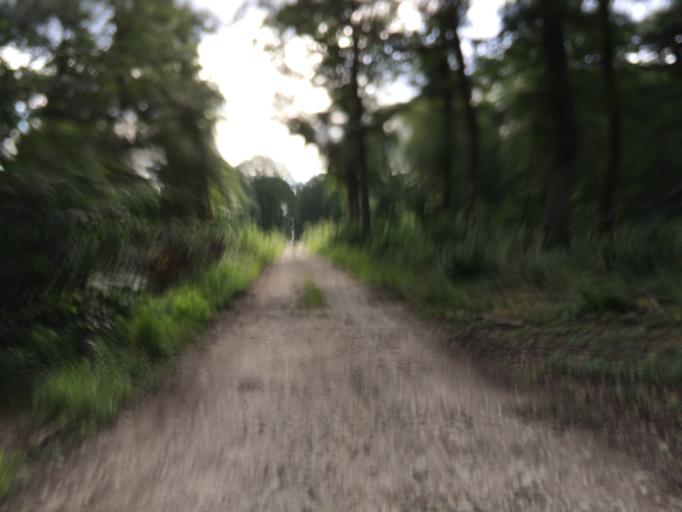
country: FR
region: Ile-de-France
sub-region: Departement de l'Essonne
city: Soisy-sur-Seine
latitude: 48.6622
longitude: 2.4425
